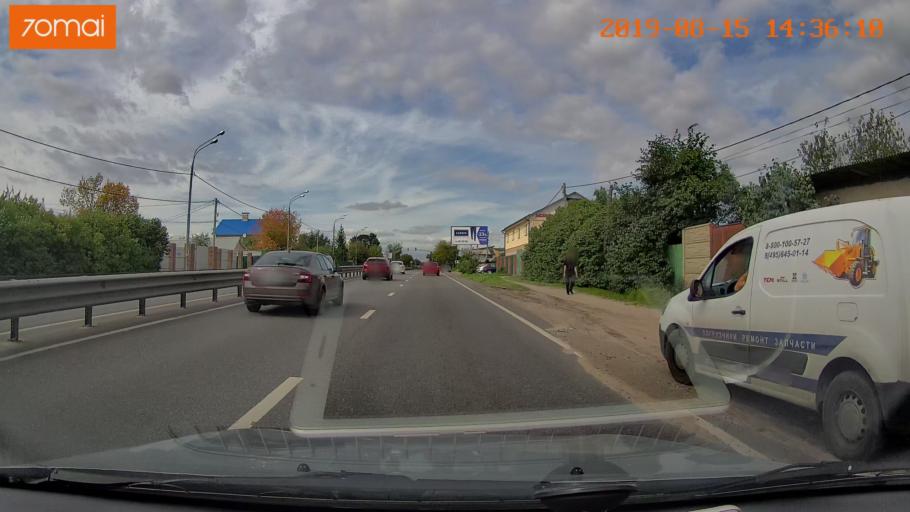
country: RU
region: Moskovskaya
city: Tomilino
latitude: 55.6441
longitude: 37.9358
